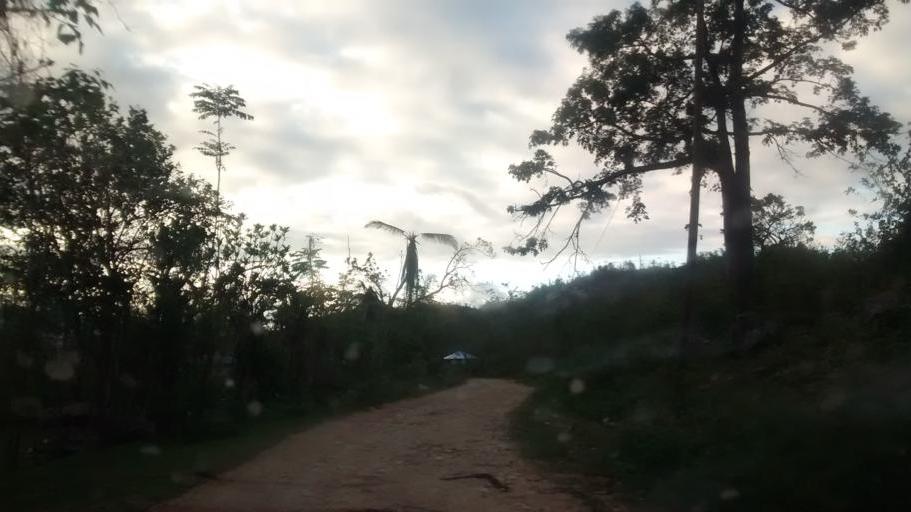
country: HT
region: Grandans
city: Corail
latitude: 18.4765
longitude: -73.7973
